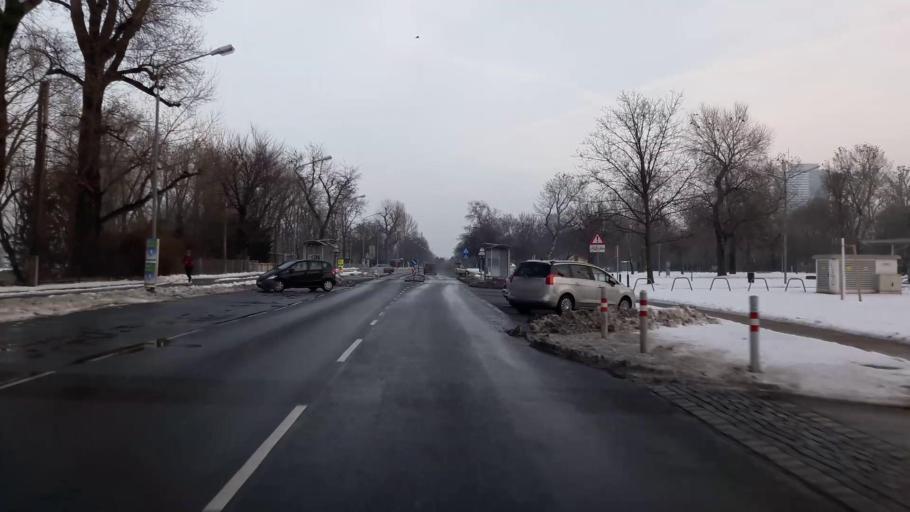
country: AT
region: Vienna
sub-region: Wien Stadt
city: Vienna
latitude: 48.2435
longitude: 16.4135
